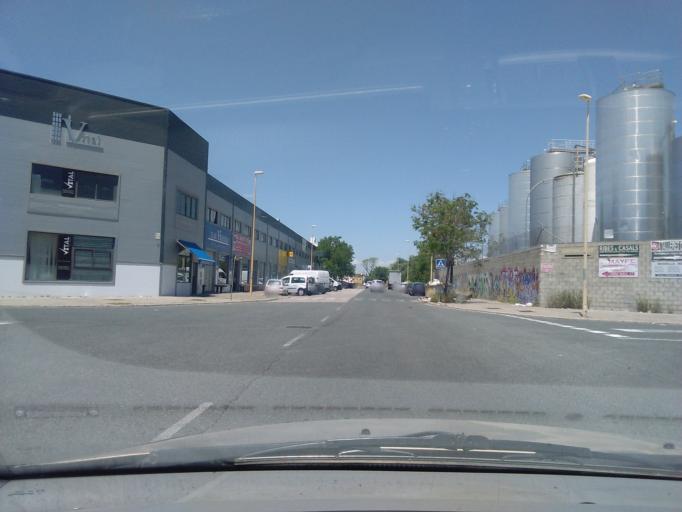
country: ES
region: Andalusia
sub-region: Provincia de Sevilla
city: Sevilla
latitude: 37.3836
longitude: -5.9302
